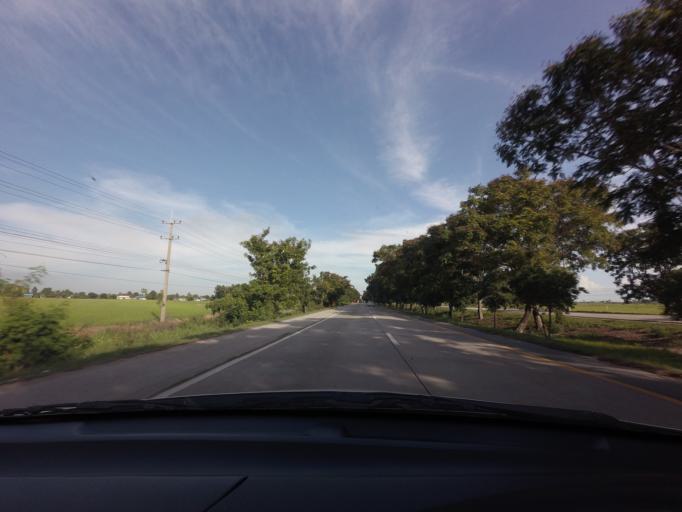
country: TH
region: Phra Nakhon Si Ayutthaya
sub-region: Amphoe Bang Sai
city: Bang Sai
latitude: 14.2912
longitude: 100.2381
